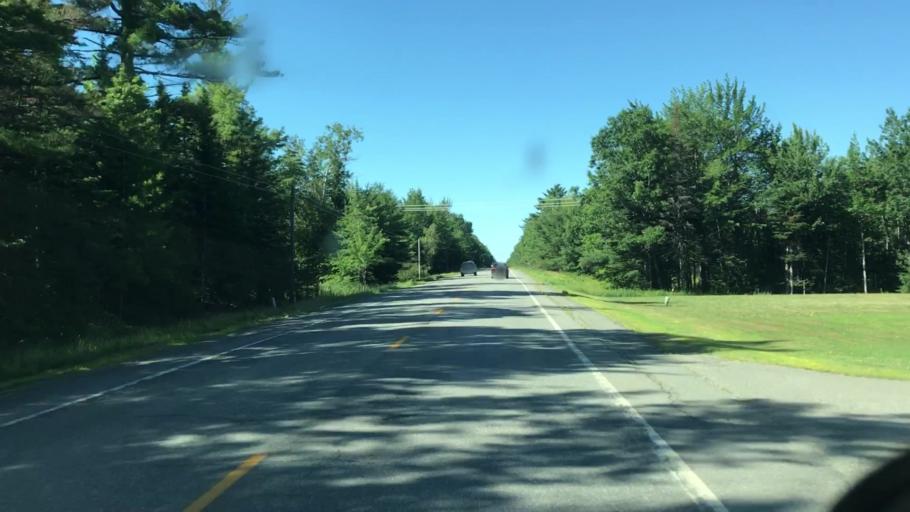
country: US
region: Maine
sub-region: Penobscot County
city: Enfield
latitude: 45.3178
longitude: -68.6015
